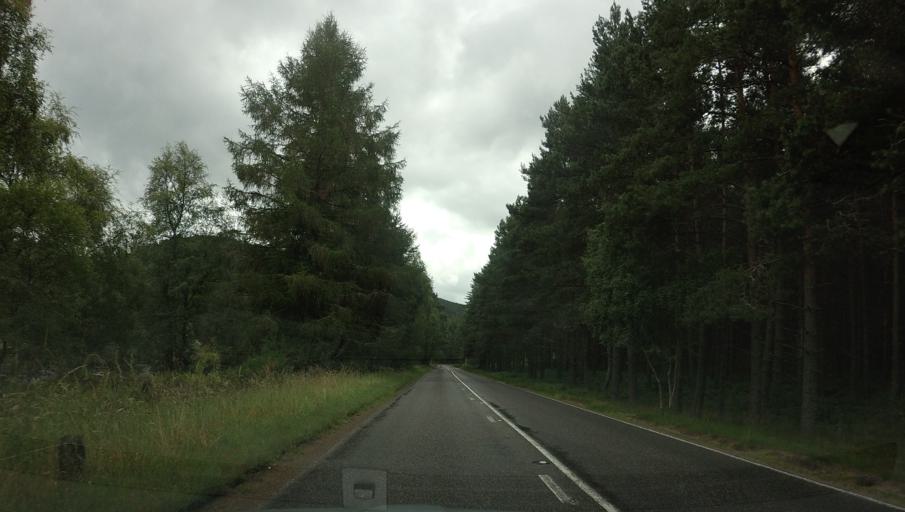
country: GB
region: Scotland
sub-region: Aberdeenshire
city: Ballater
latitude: 57.0130
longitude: -3.2975
